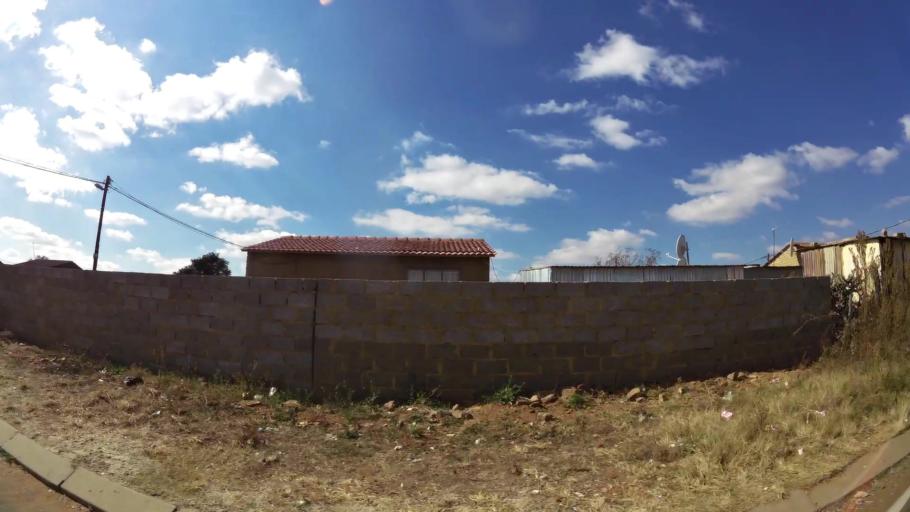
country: ZA
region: Gauteng
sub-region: West Rand District Municipality
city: Krugersdorp
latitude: -26.1451
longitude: 27.7823
